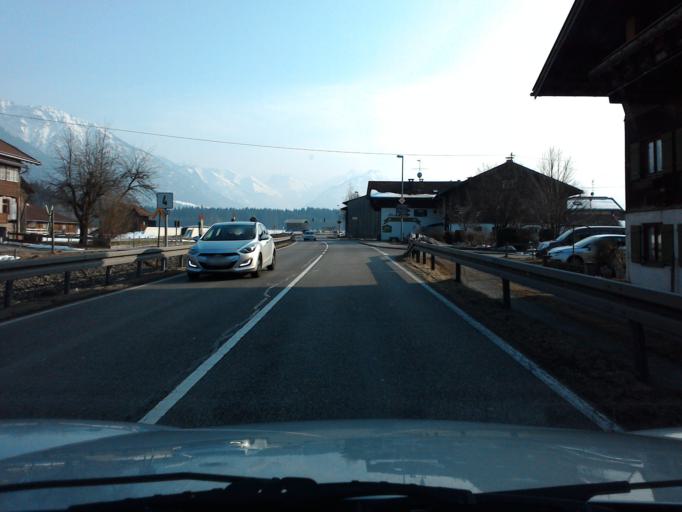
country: DE
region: Bavaria
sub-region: Swabia
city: Oberstdorf
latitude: 47.4401
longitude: 10.2755
